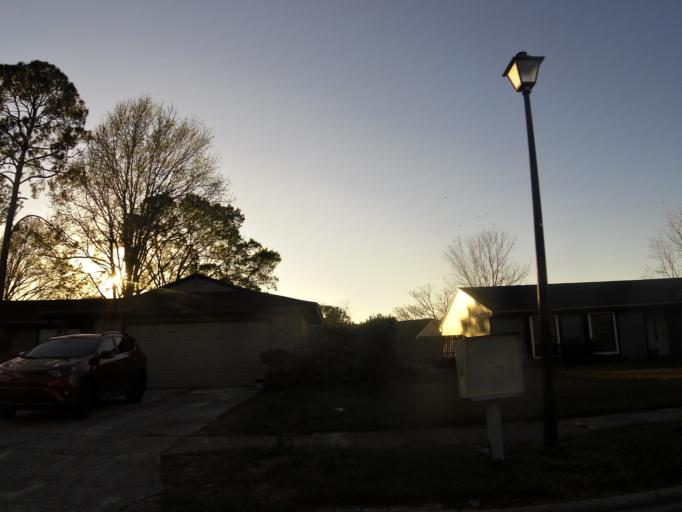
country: US
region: Florida
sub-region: Saint Johns County
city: Fruit Cove
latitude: 30.1752
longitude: -81.5833
